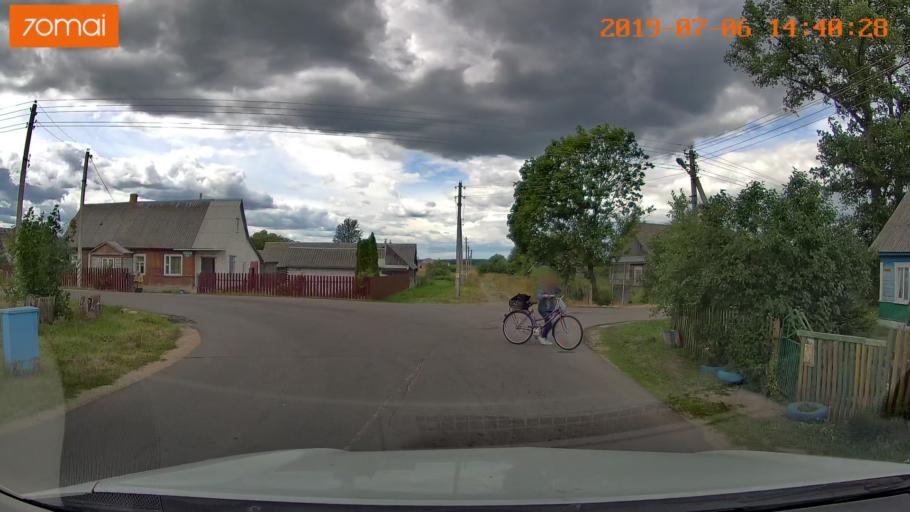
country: BY
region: Minsk
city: Ivyanyets
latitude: 53.9247
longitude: 26.6736
